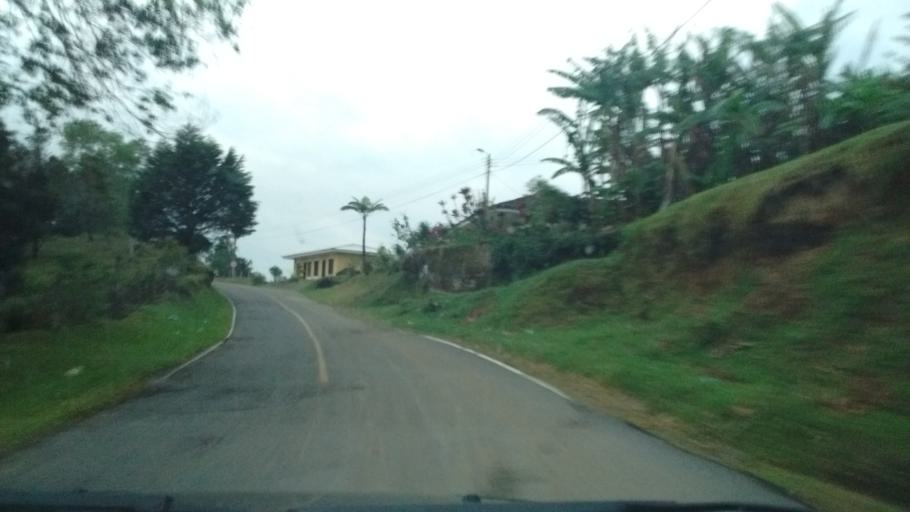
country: CO
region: Cauca
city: Lopez
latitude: 2.3788
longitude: -76.7090
